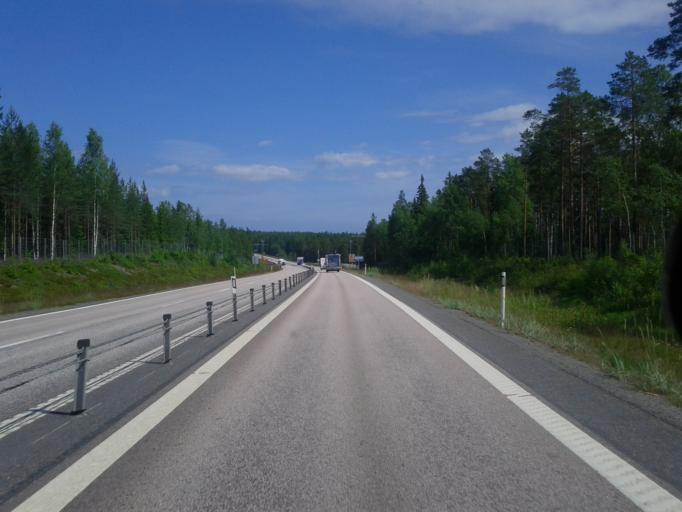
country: SE
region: Vaesternorrland
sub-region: OErnskoeldsviks Kommun
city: Husum
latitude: 63.4592
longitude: 19.2542
